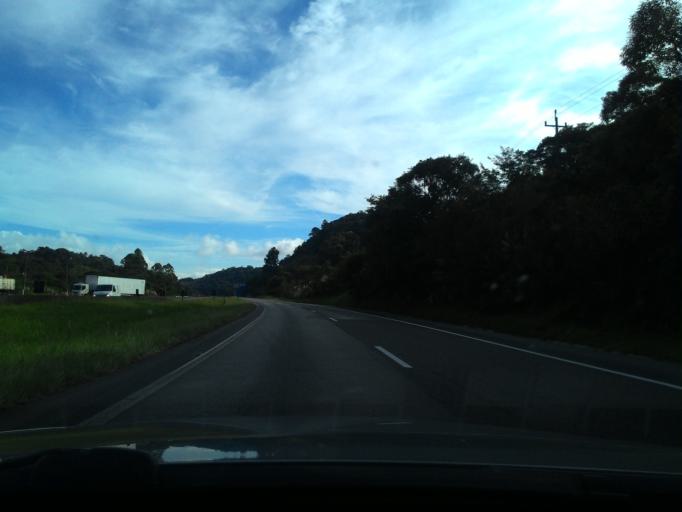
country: BR
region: Parana
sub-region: Campina Grande Do Sul
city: Campina Grande do Sul
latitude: -25.2500
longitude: -48.9094
